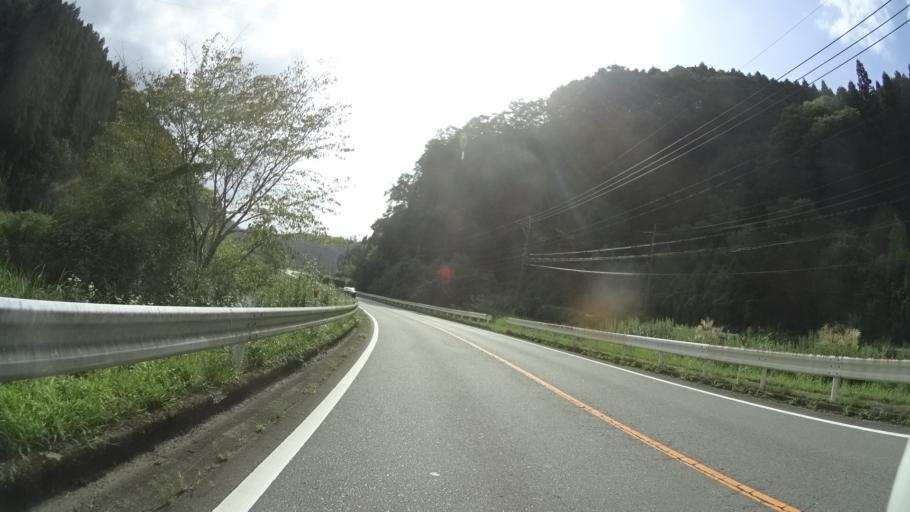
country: JP
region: Kumamoto
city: Aso
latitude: 32.6950
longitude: 131.1012
